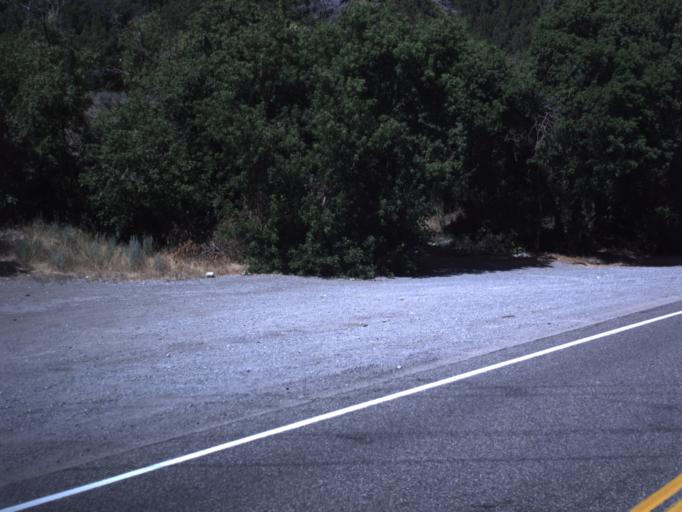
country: US
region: Utah
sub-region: Cache County
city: North Logan
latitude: 41.7436
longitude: -111.7597
